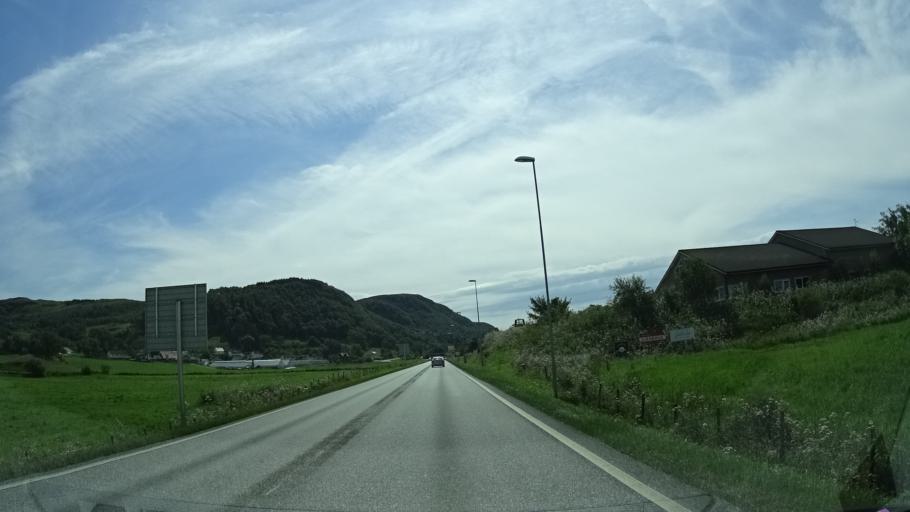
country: NO
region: Rogaland
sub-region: Rennesoy
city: Vikevag
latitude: 59.1116
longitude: 5.6987
